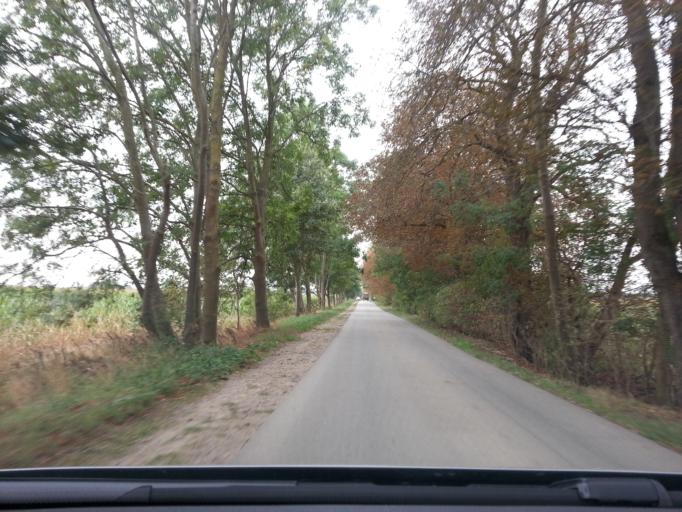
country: DE
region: Mecklenburg-Vorpommern
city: Ferdinandshof
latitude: 53.6696
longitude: 13.9163
